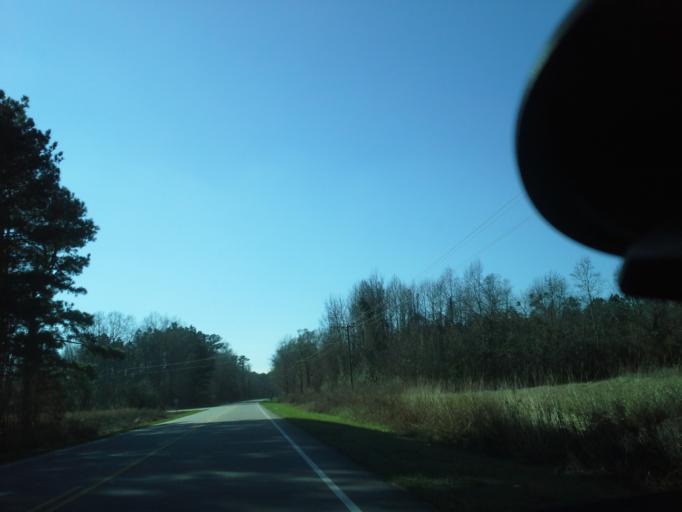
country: US
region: North Carolina
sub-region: Beaufort County
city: Belhaven
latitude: 35.5831
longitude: -76.6669
